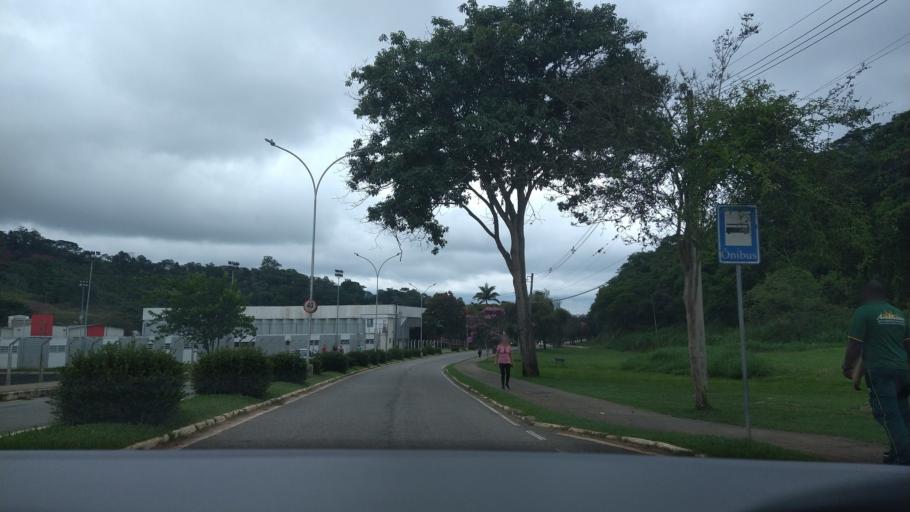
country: BR
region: Minas Gerais
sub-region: Vicosa
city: Vicosa
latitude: -20.7668
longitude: -42.8614
